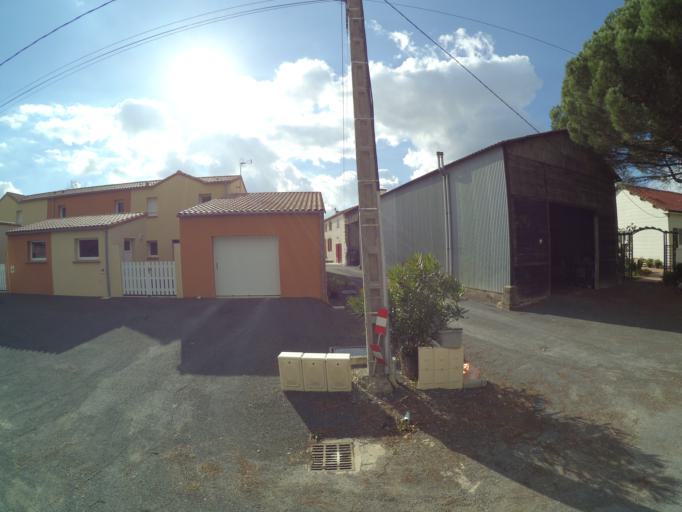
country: FR
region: Pays de la Loire
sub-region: Departement de la Loire-Atlantique
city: Remouille
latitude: 47.0698
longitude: -1.3582
